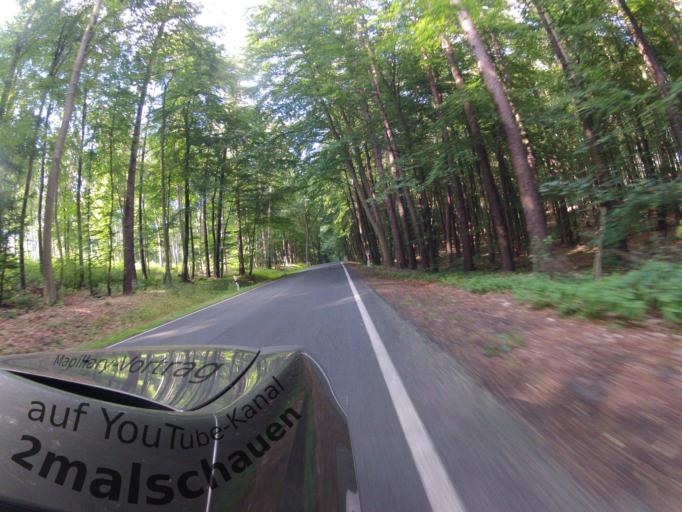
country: DE
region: Mecklenburg-Vorpommern
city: Seebad Heringsdorf
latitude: 53.9220
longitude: 14.1714
